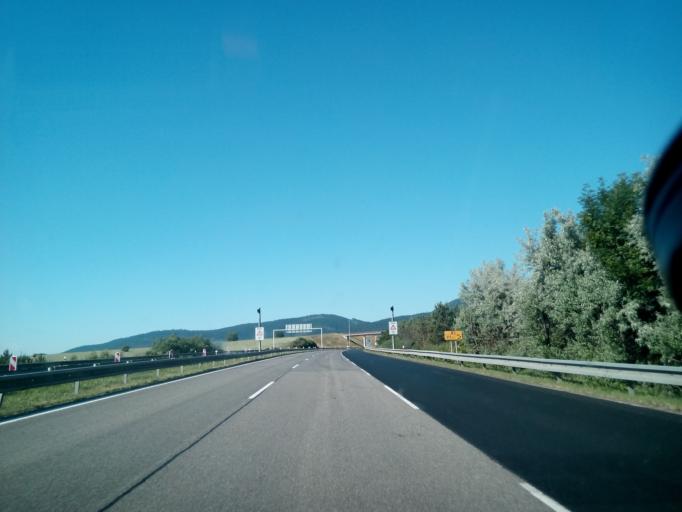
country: SK
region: Kosicky
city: Krompachy
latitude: 49.0014
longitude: 20.9307
